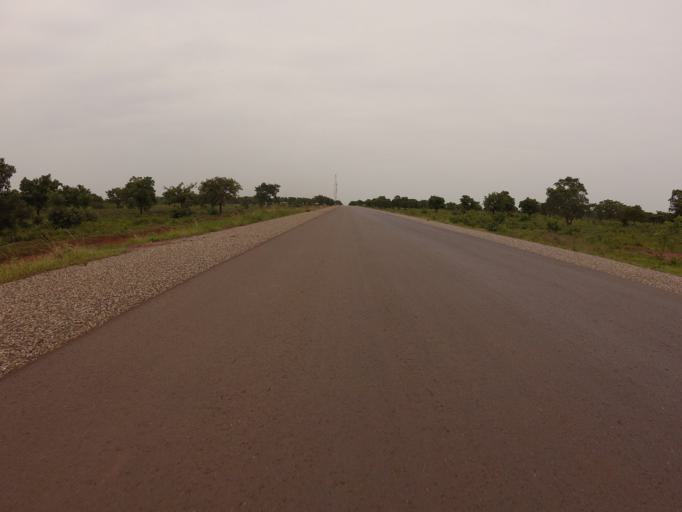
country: GH
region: Northern
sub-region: Yendi
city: Yendi
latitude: 9.2902
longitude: 0.0180
